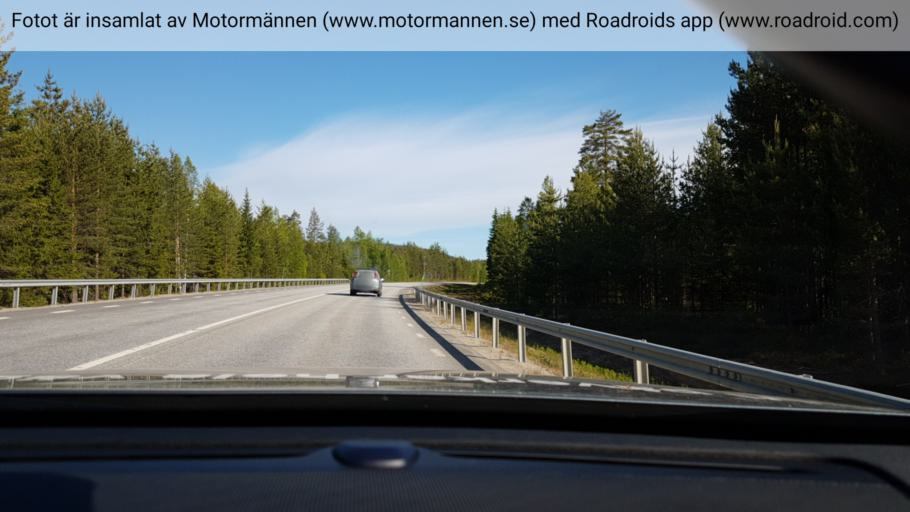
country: SE
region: Vaesterbotten
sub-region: Vannas Kommun
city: Vaennaes
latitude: 64.0107
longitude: 19.6965
